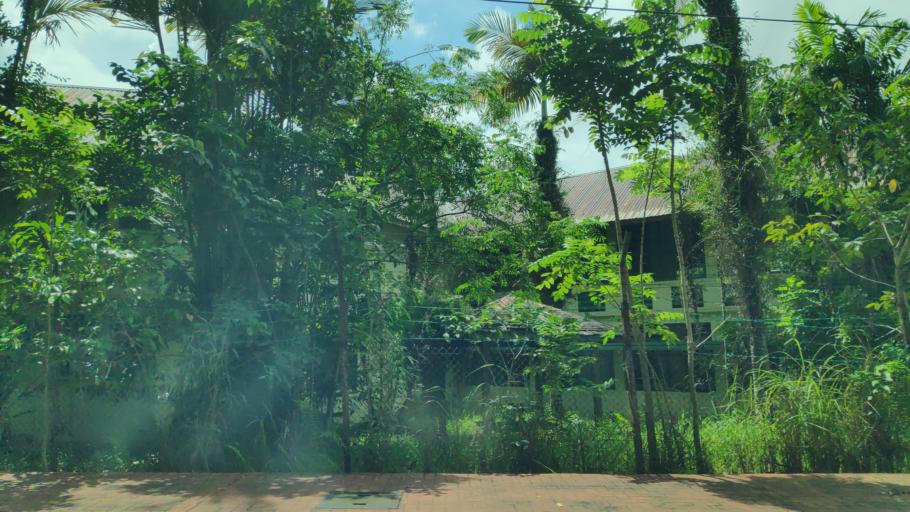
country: MY
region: Sarawak
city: Kuching
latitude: 1.5438
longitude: 110.3420
